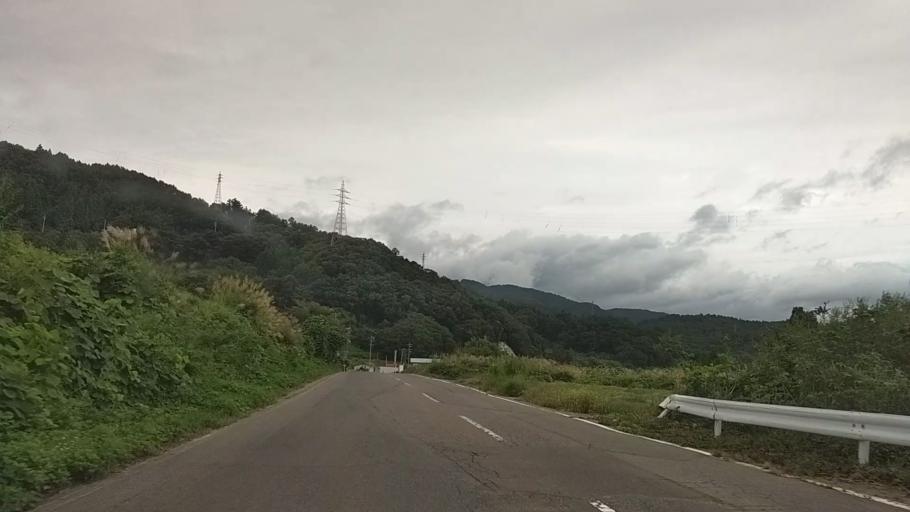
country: JP
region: Nagano
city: Nakano
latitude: 36.7957
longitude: 138.3454
